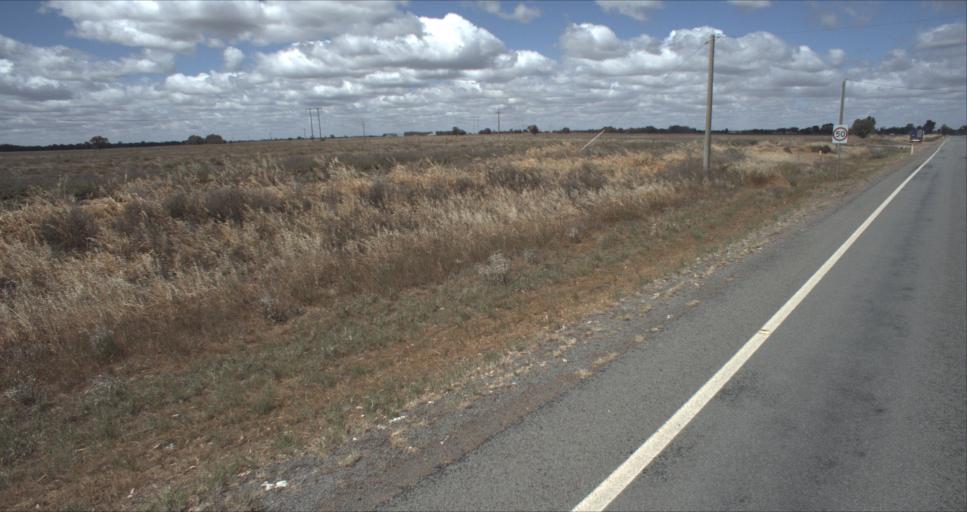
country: AU
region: New South Wales
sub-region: Murrumbidgee Shire
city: Darlington Point
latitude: -34.5095
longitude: 146.1866
